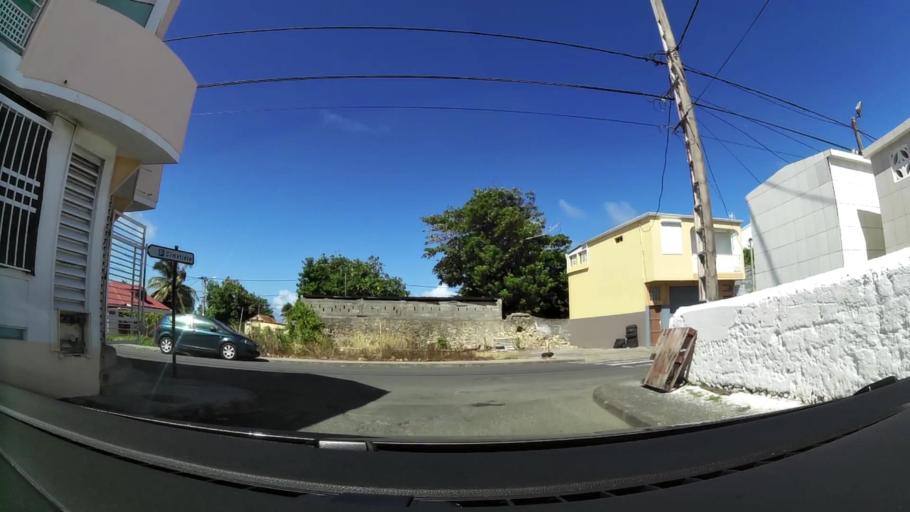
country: GP
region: Guadeloupe
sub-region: Guadeloupe
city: Le Moule
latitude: 16.3311
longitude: -61.3479
